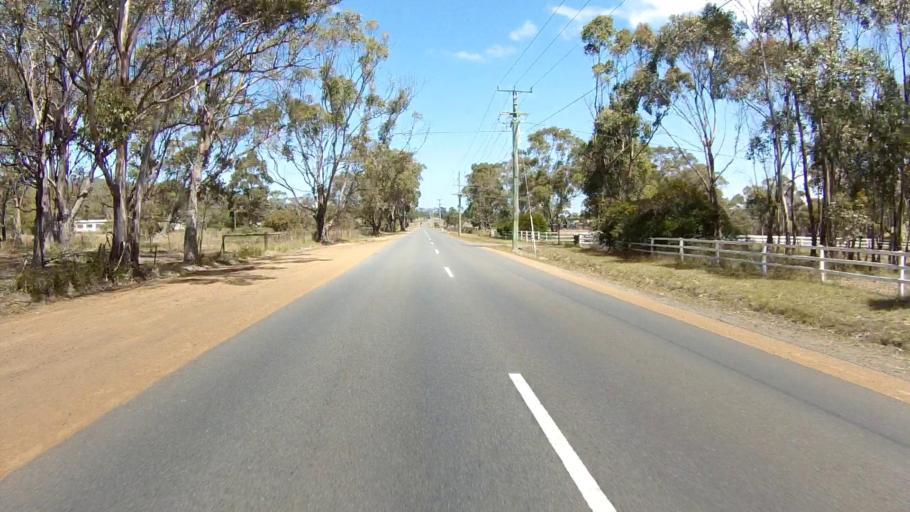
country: AU
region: Tasmania
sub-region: Clarence
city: Sandford
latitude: -42.9469
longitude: 147.4821
